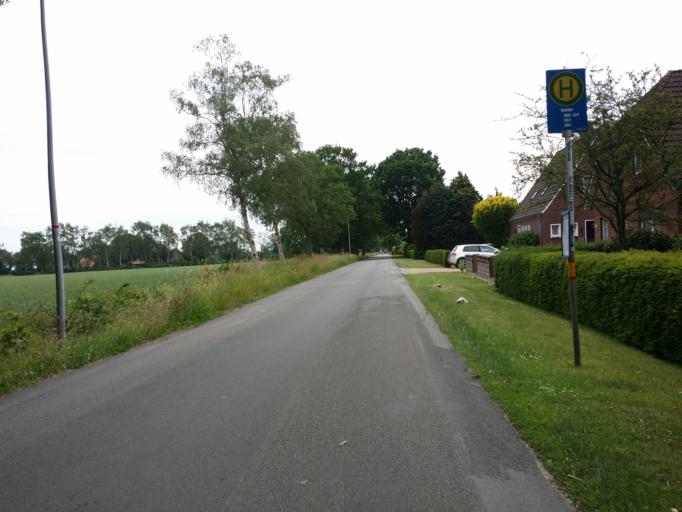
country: DE
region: Lower Saxony
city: Bockhorn
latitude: 53.3395
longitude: 8.0312
